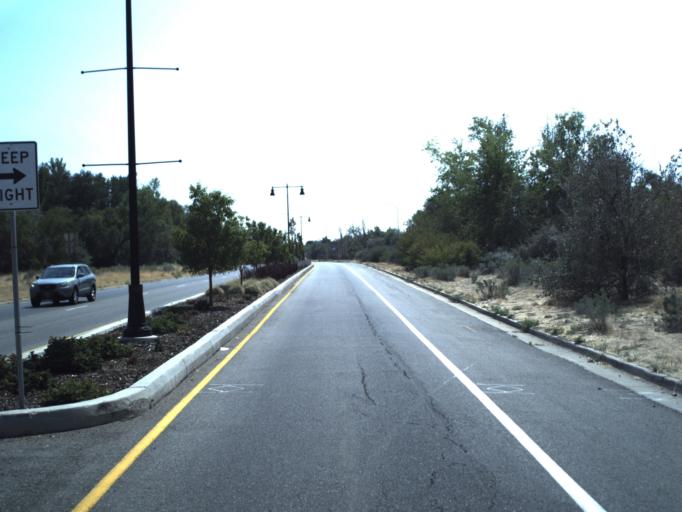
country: US
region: Utah
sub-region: Salt Lake County
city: Little Cottonwood Creek Valley
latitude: 40.6295
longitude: -111.8625
